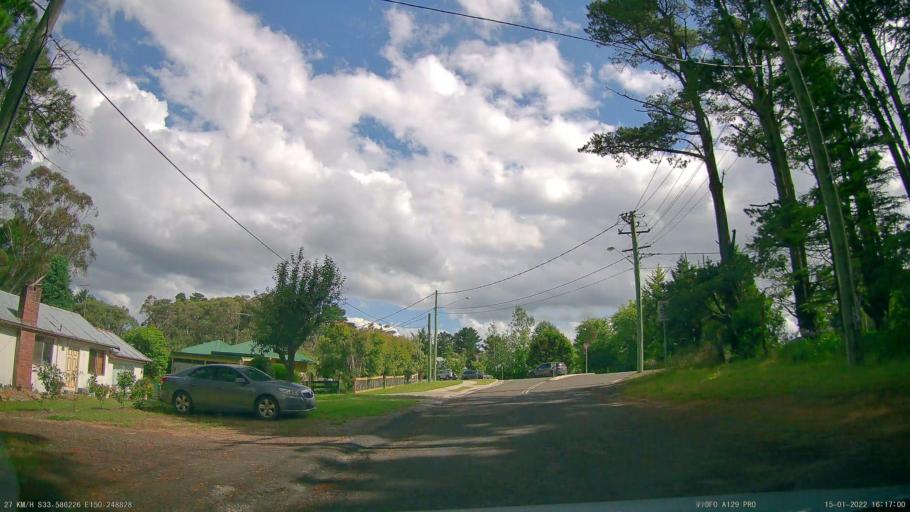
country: AU
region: New South Wales
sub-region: Blue Mountains Municipality
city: Blackheath
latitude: -33.5863
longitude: 150.2488
